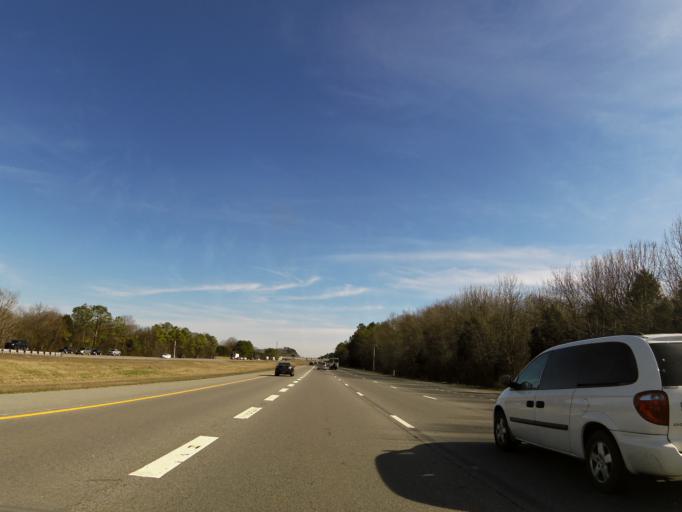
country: US
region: Tennessee
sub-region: Rutherford County
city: Smyrna
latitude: 35.9312
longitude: -86.5285
